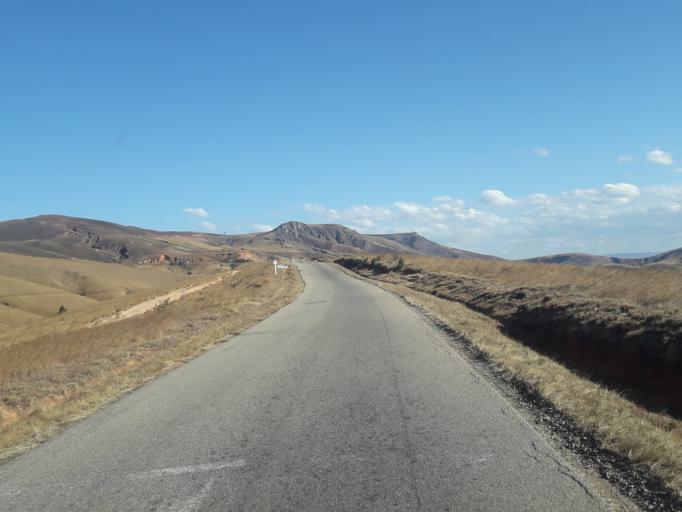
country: MG
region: Analamanga
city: Ankazobe
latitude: -17.8001
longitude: 47.0214
